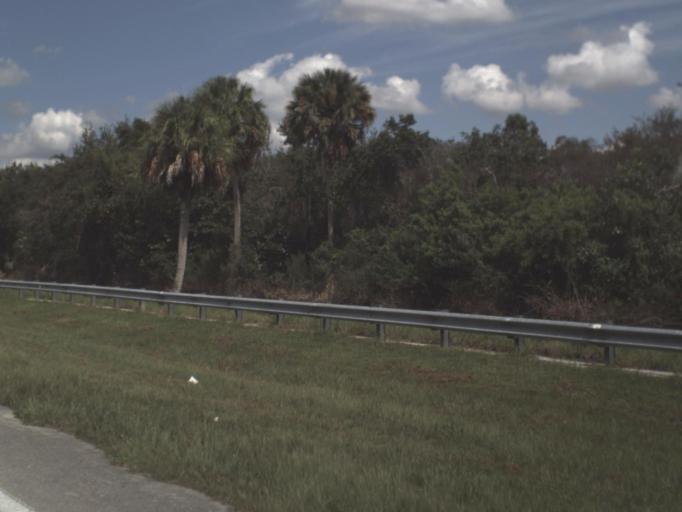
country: US
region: Florida
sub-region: Collier County
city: Orangetree
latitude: 26.1211
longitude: -81.3448
